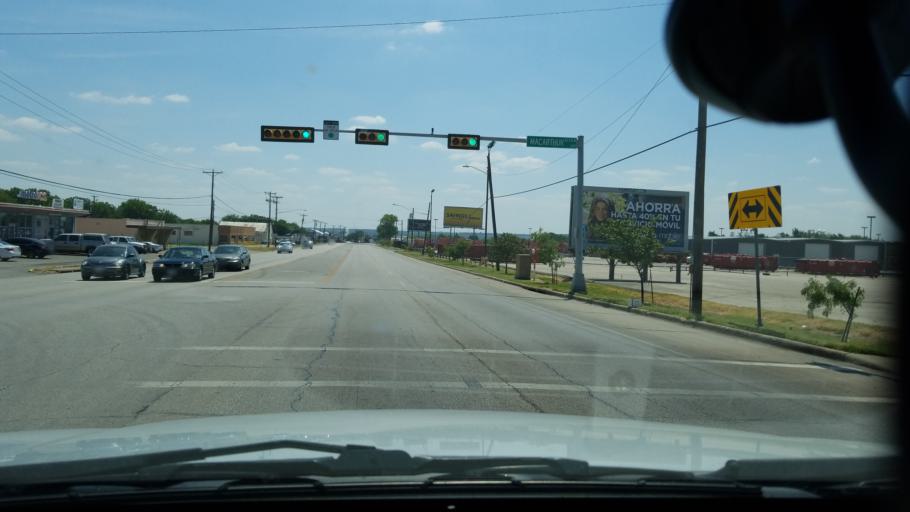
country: US
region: Texas
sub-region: Dallas County
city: Grand Prairie
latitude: 32.7494
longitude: -96.9606
